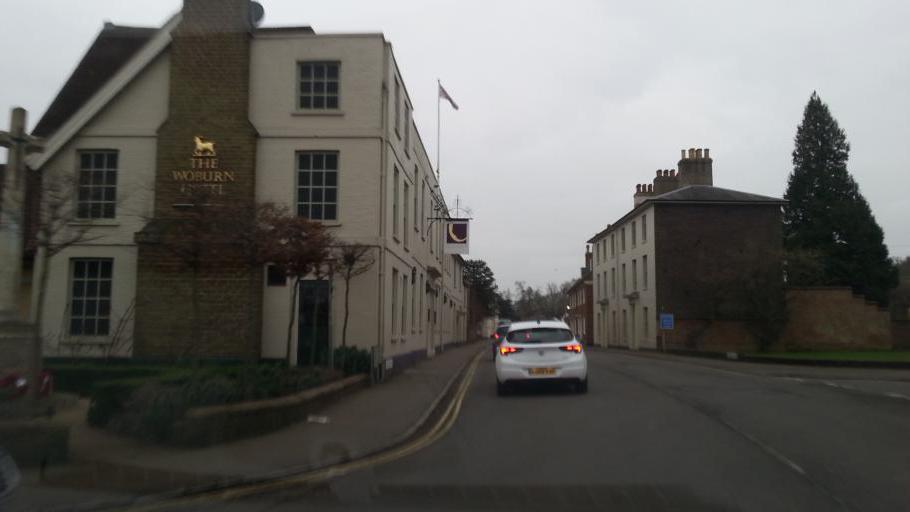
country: GB
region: England
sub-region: Central Bedfordshire
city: Woburn
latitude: 51.9888
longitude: -0.6190
